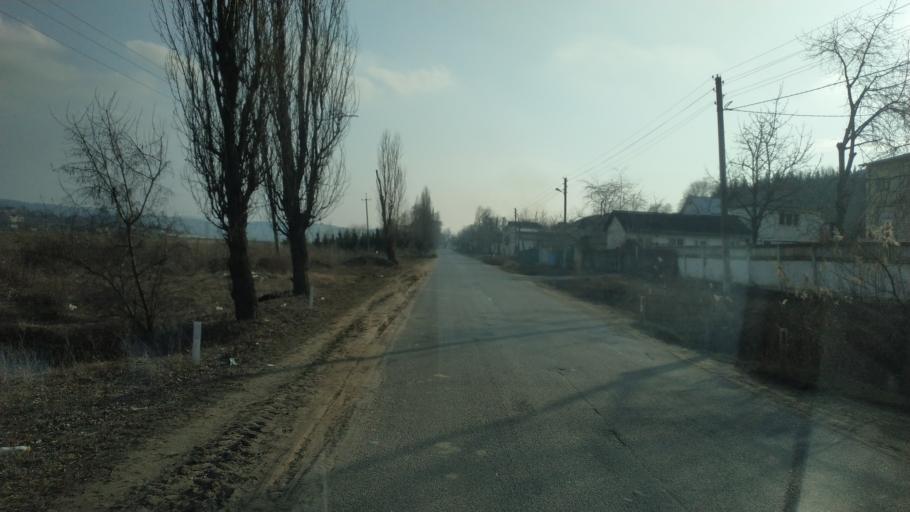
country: MD
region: Hincesti
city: Dancu
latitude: 46.7818
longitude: 28.3489
